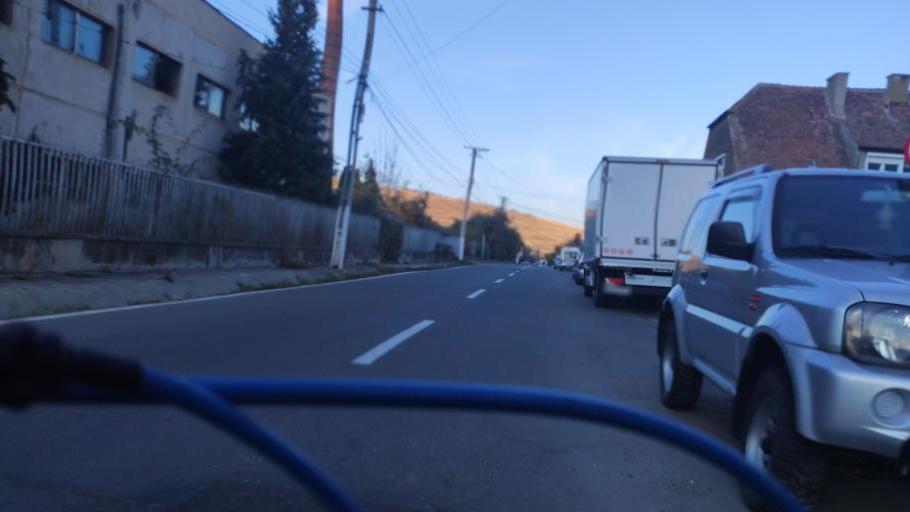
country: RO
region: Brasov
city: Codlea
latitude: 45.7042
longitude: 25.4421
